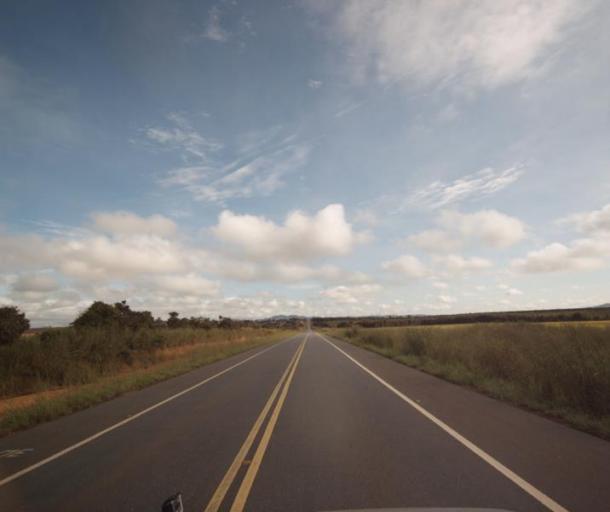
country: BR
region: Goias
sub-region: Barro Alto
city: Barro Alto
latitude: -15.2253
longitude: -48.6954
